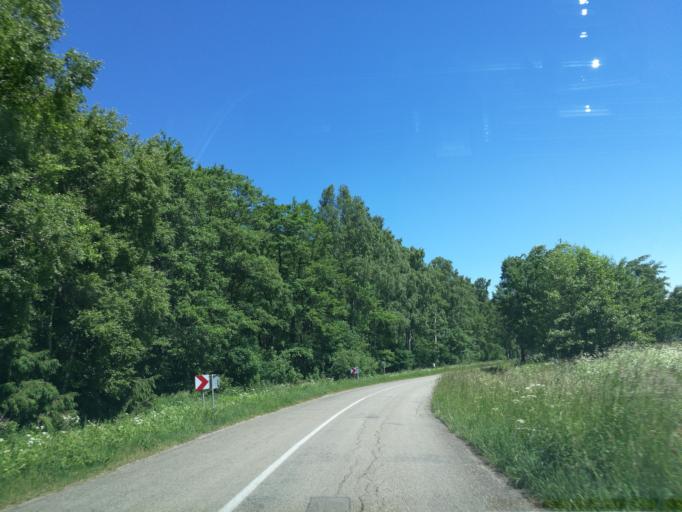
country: LT
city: Neringa
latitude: 55.3835
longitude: 21.2322
